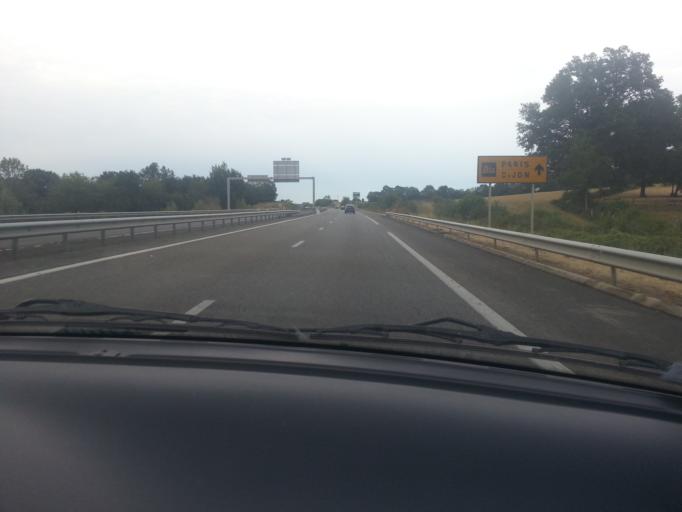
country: FR
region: Bourgogne
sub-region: Departement de Saone-et-Loire
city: Paray-le-Monial
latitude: 46.4712
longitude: 4.1279
